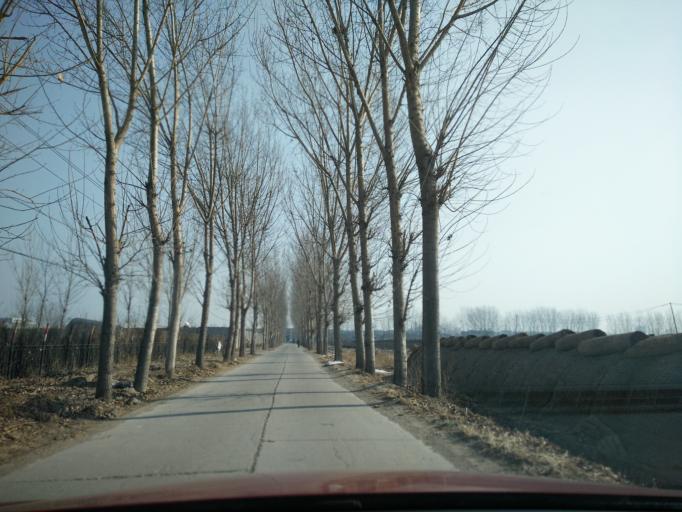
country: CN
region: Beijing
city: Yinghai
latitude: 39.7143
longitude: 116.4473
